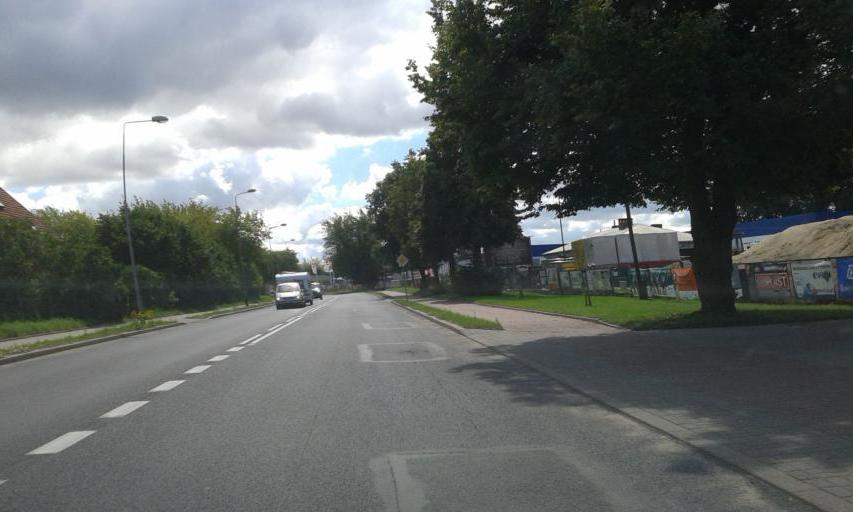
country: PL
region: West Pomeranian Voivodeship
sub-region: Powiat walecki
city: Walcz
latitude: 53.2653
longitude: 16.4889
